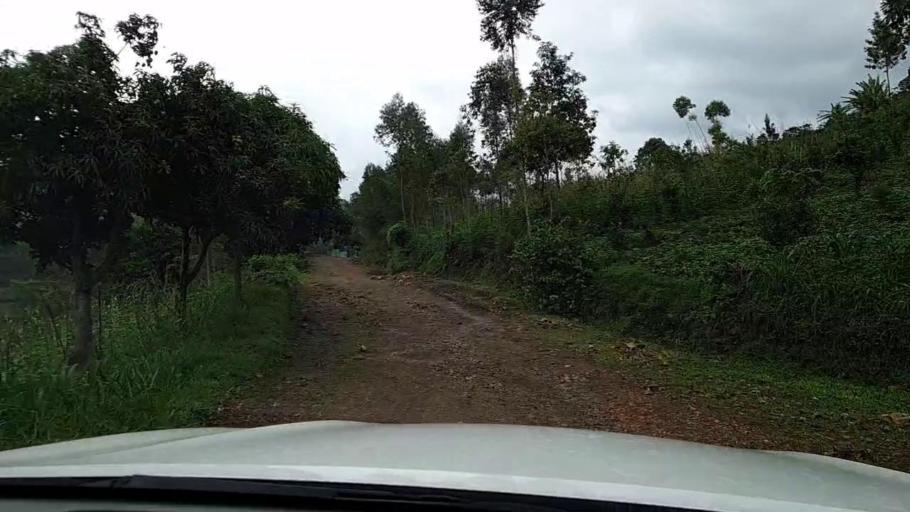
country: RW
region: Western Province
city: Cyangugu
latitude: -2.5596
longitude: 29.0357
